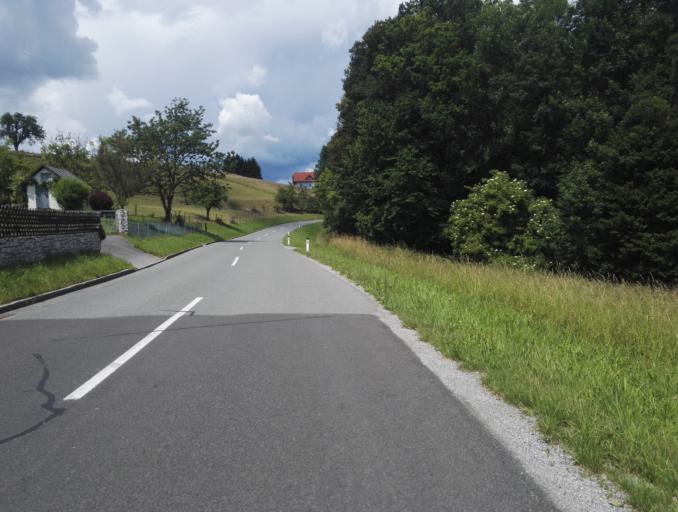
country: AT
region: Styria
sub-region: Politischer Bezirk Graz-Umgebung
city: Sankt Oswald bei Plankenwarth
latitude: 47.0867
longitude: 15.2947
